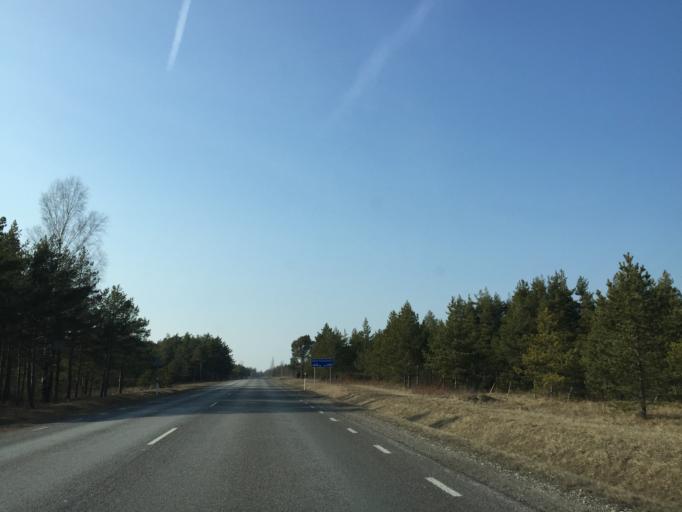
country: EE
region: Saare
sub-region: Orissaare vald
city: Orissaare
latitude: 58.5764
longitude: 23.3704
